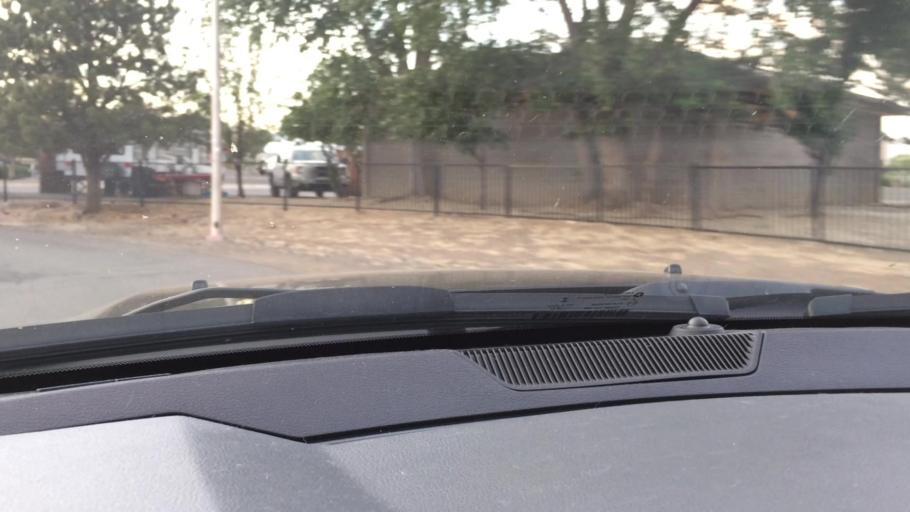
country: US
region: Nevada
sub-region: Washoe County
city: Sparks
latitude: 39.5218
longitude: -119.7742
